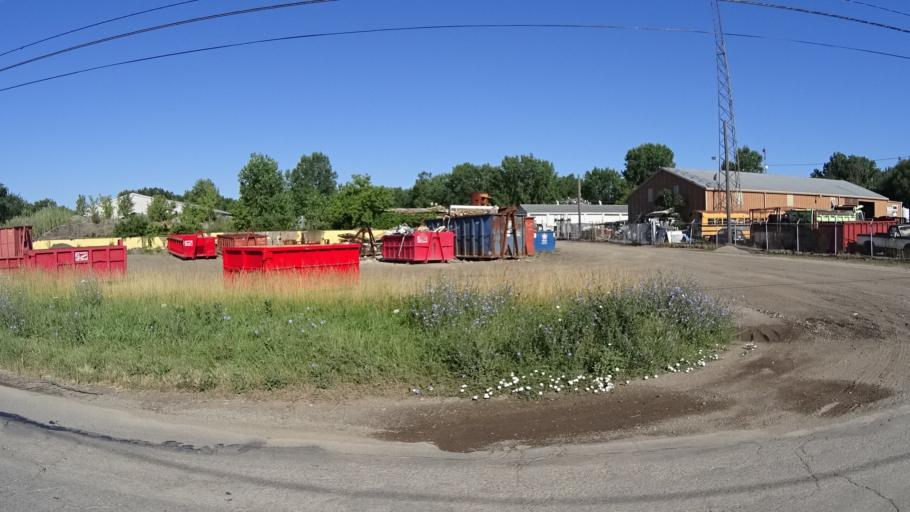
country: US
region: Ohio
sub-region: Erie County
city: Sandusky
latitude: 41.4273
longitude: -82.7320
